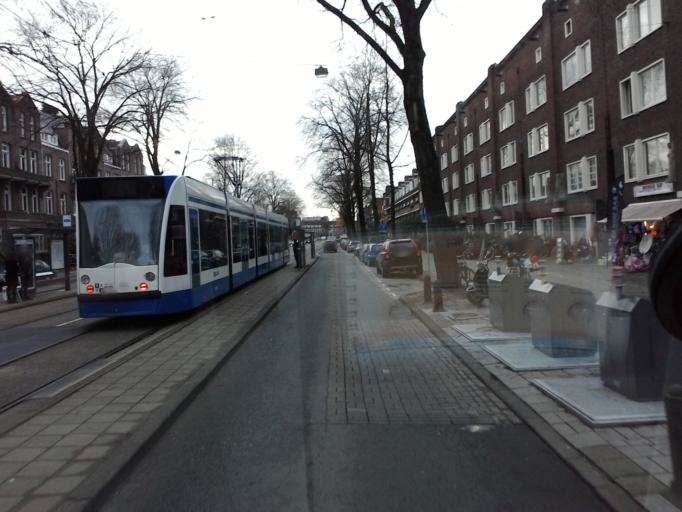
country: NL
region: North Holland
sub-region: Gemeente Amsterdam
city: Amsterdam
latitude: 52.3619
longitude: 4.8532
